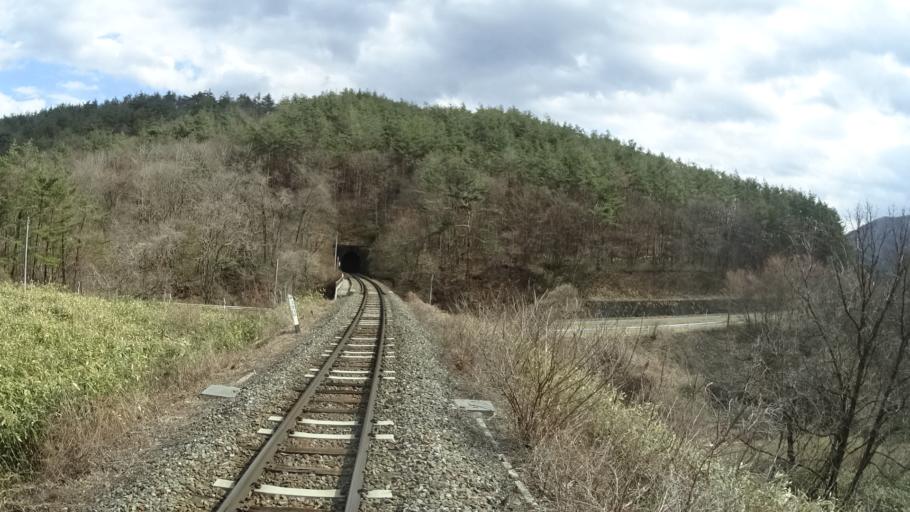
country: JP
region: Iwate
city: Tono
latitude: 39.3145
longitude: 141.3716
